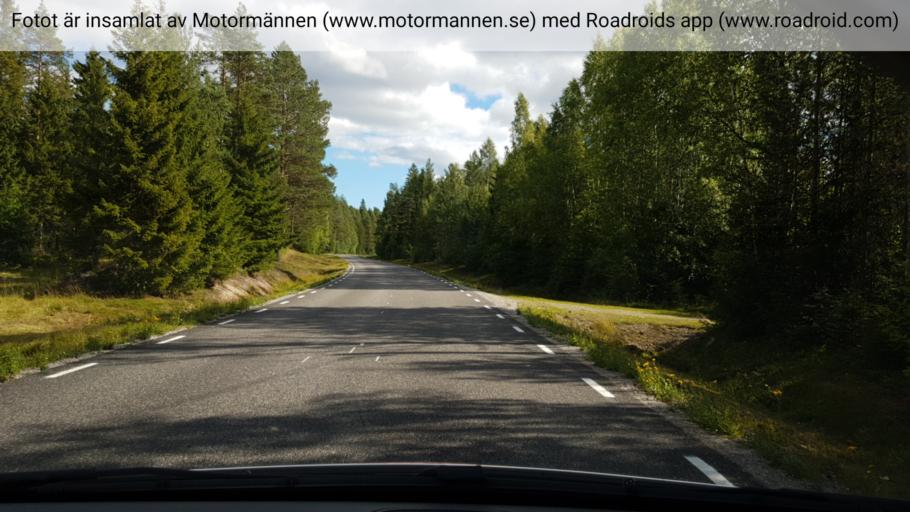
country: SE
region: Vaesterbotten
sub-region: Umea Kommun
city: Hoernefors
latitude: 63.6808
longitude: 19.9103
